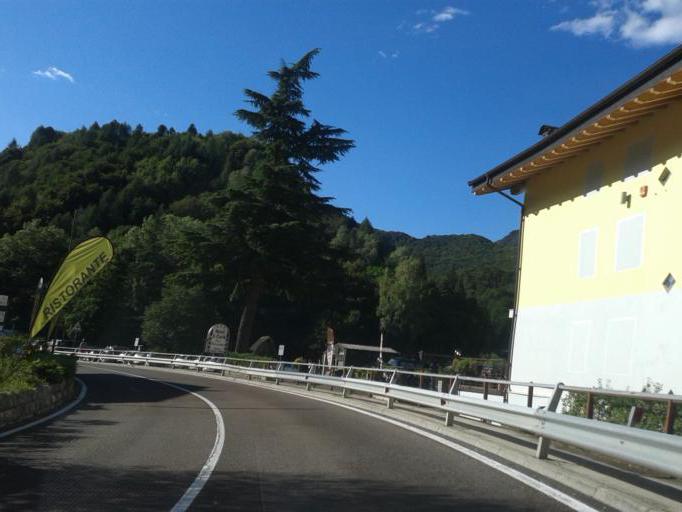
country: IT
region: Trentino-Alto Adige
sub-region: Provincia di Trento
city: Molina di Ledro
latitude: 45.8749
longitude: 10.7661
